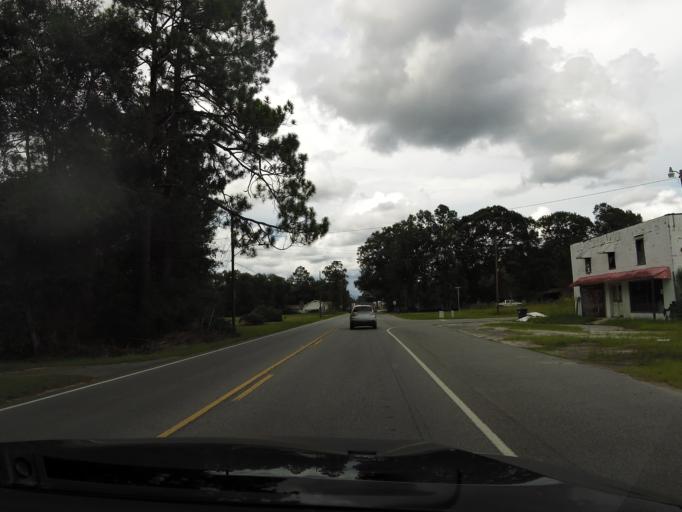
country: US
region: Georgia
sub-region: Brantley County
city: Nahunta
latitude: 31.1980
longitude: -81.9842
